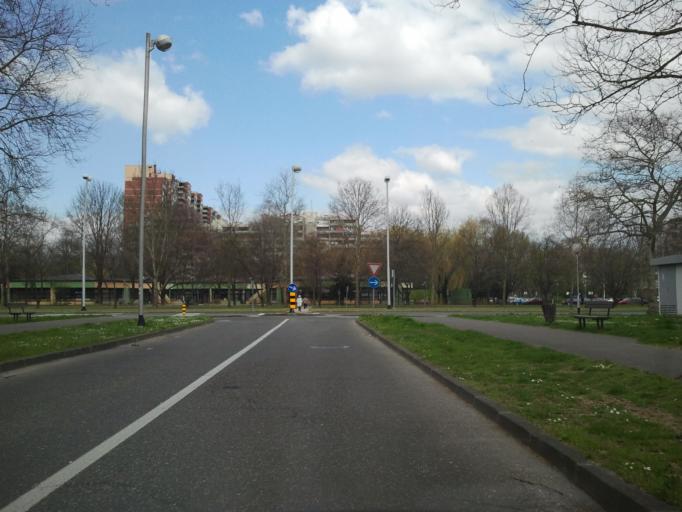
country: HR
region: Grad Zagreb
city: Novi Zagreb
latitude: 45.7672
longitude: 15.9958
